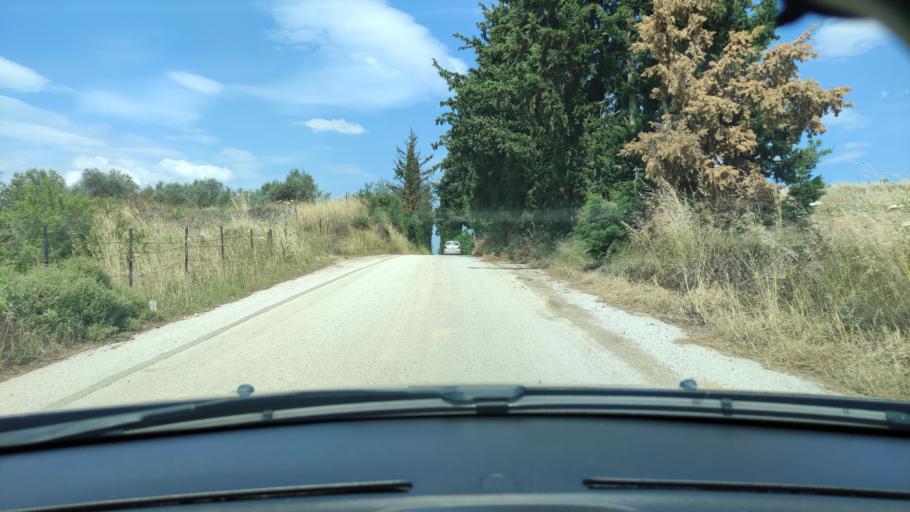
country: GR
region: Central Greece
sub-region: Nomos Evvoias
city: Afration
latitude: 38.5188
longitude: 23.7650
